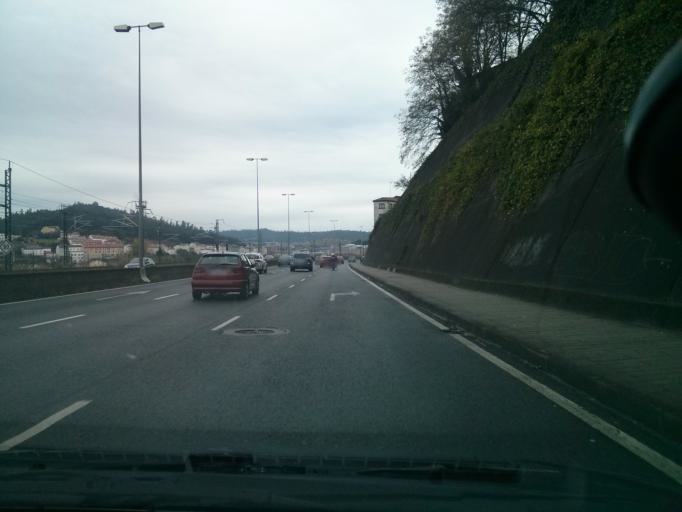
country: ES
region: Galicia
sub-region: Provincia da Coruna
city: Santiago de Compostela
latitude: 42.8759
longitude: -8.5354
